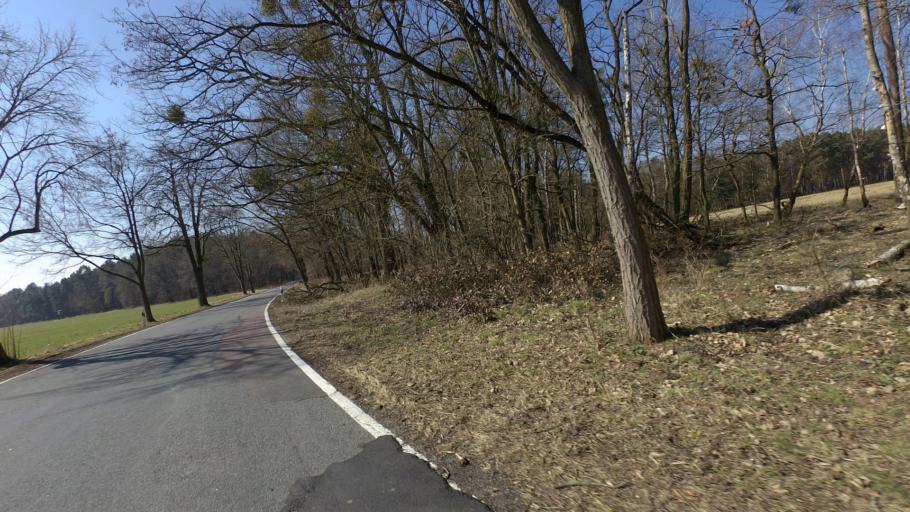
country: DE
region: Saxony-Anhalt
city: Coswig
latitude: 51.9071
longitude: 12.5156
